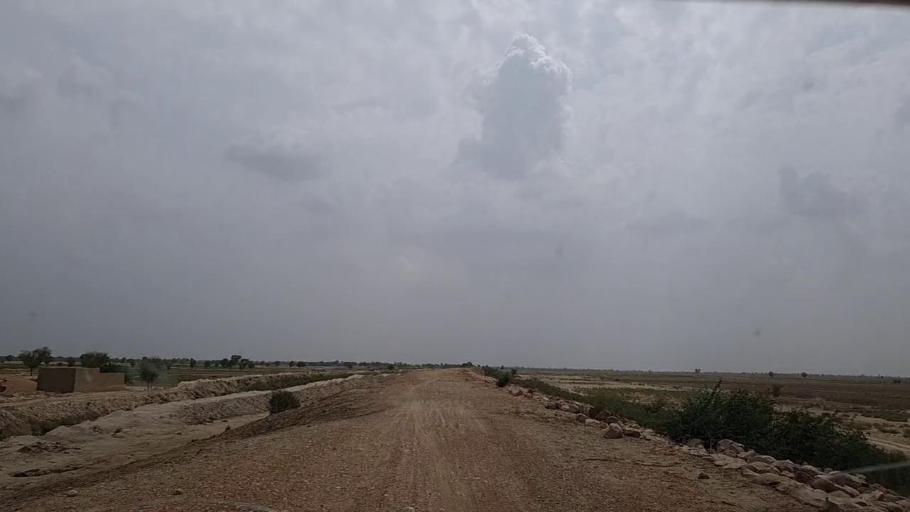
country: PK
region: Sindh
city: Johi
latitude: 26.7472
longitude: 67.5888
